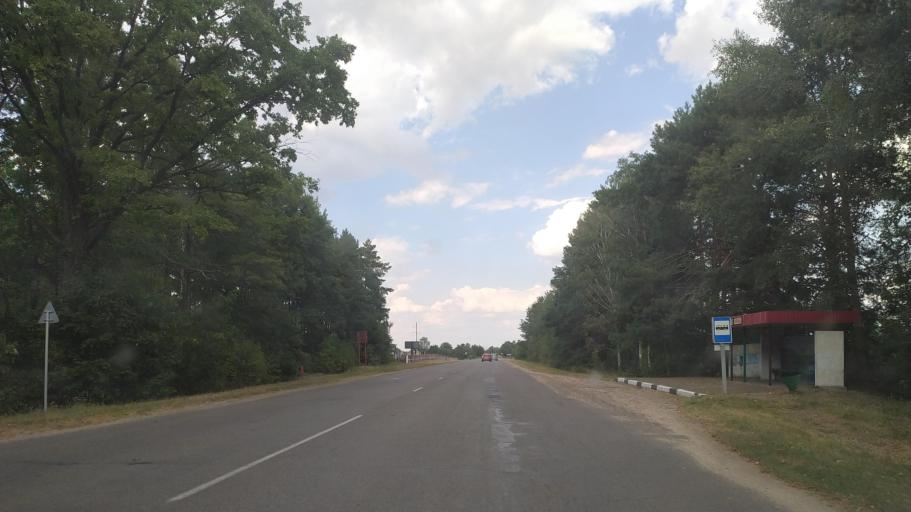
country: BY
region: Brest
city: Drahichyn
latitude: 52.1084
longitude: 25.1146
